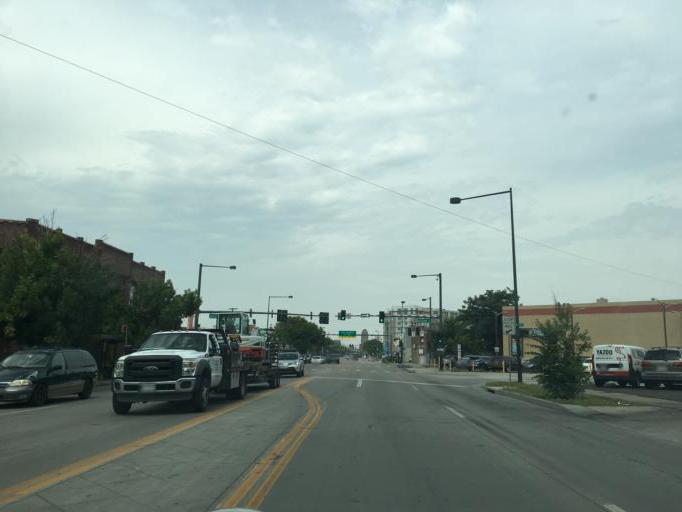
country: US
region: Colorado
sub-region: Denver County
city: Denver
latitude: 39.7521
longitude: -104.9874
